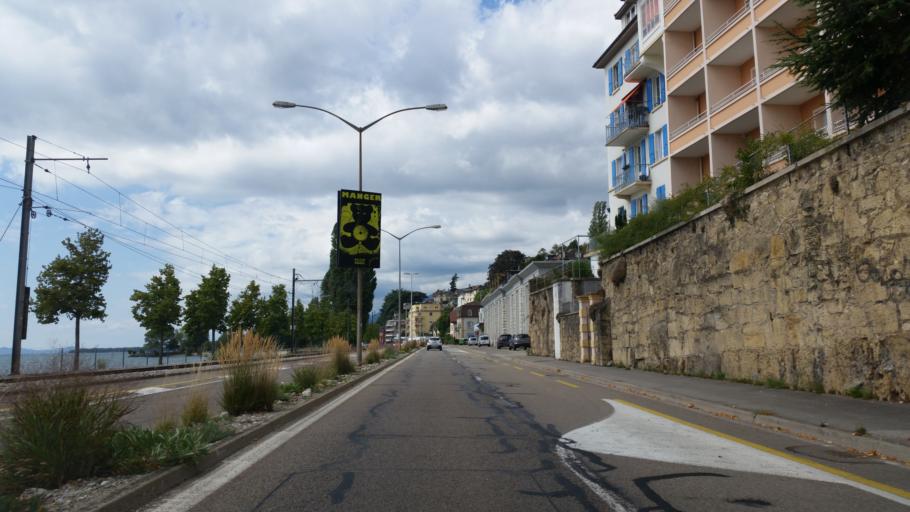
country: CH
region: Neuchatel
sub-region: Neuchatel District
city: Neuchatel
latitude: 46.9872
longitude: 6.9175
